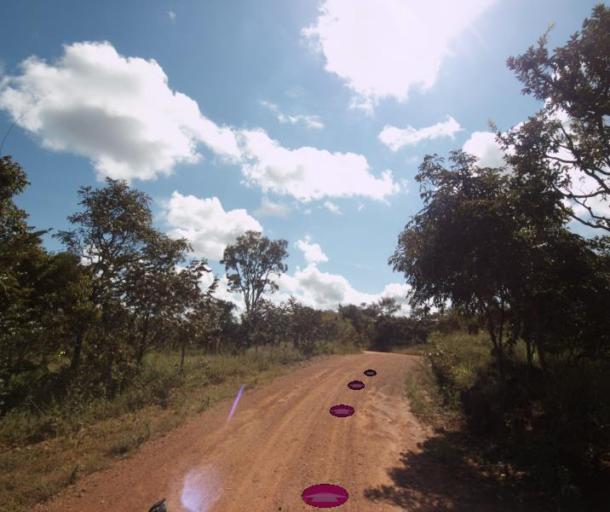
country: BR
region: Goias
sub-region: Pirenopolis
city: Pirenopolis
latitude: -15.7746
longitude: -48.9957
